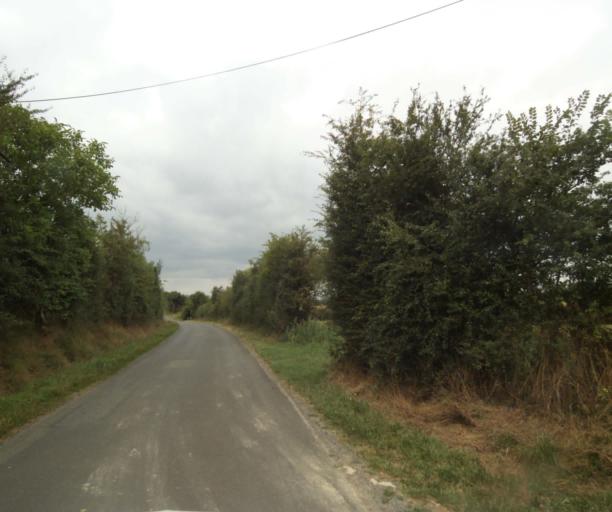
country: FR
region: Pays de la Loire
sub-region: Departement de la Sarthe
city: Juigne-sur-Sarthe
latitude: 47.8543
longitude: -0.2716
